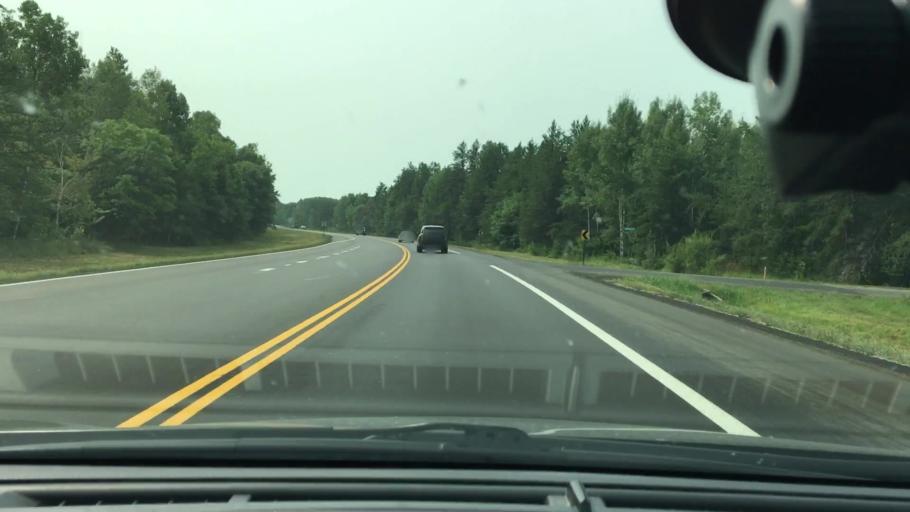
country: US
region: Minnesota
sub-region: Crow Wing County
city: Brainerd
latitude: 46.4245
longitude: -94.1782
